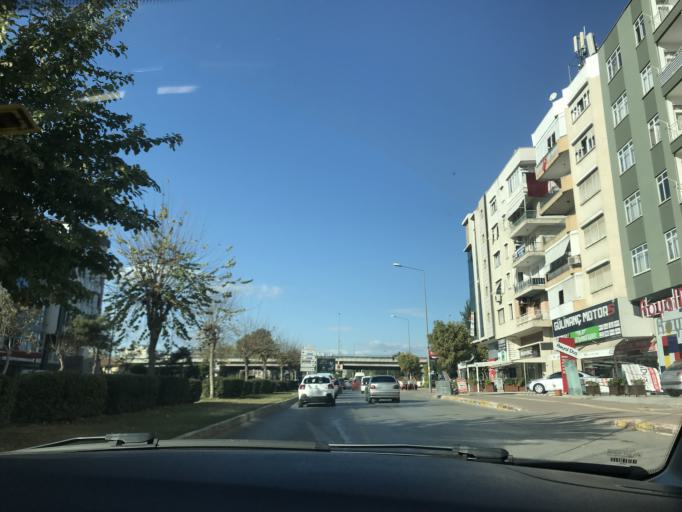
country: TR
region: Antalya
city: Antalya
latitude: 36.9094
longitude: 30.6986
